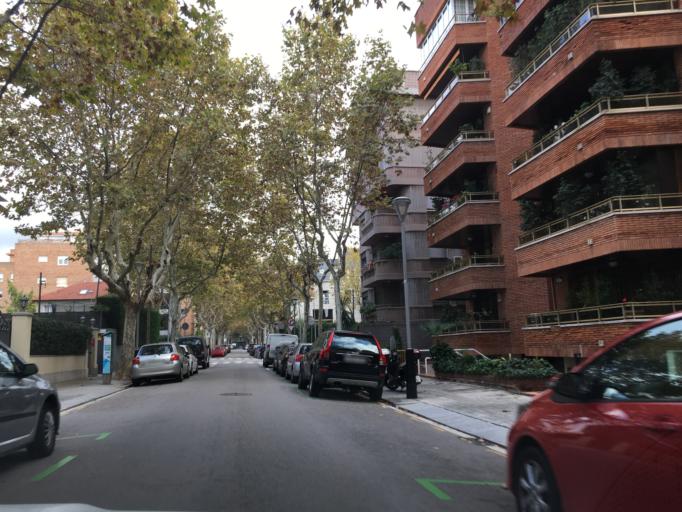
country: ES
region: Catalonia
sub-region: Provincia de Barcelona
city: Sarria-Sant Gervasi
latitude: 41.4003
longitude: 2.1284
